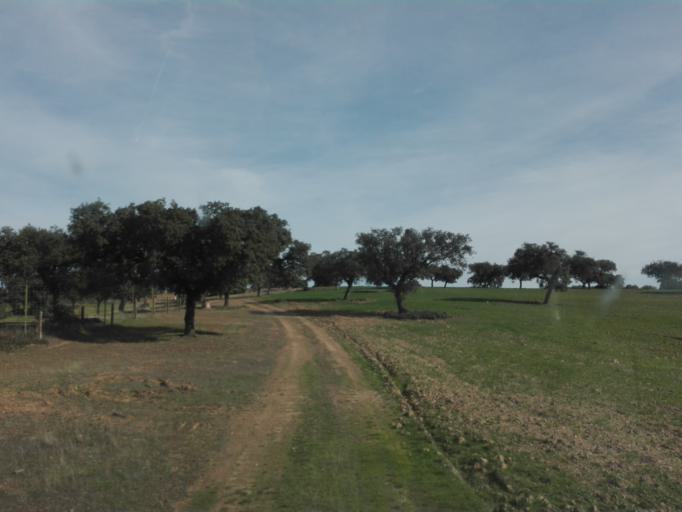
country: ES
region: Extremadura
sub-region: Provincia de Badajoz
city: Azuaga
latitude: 38.2197
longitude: -5.7411
